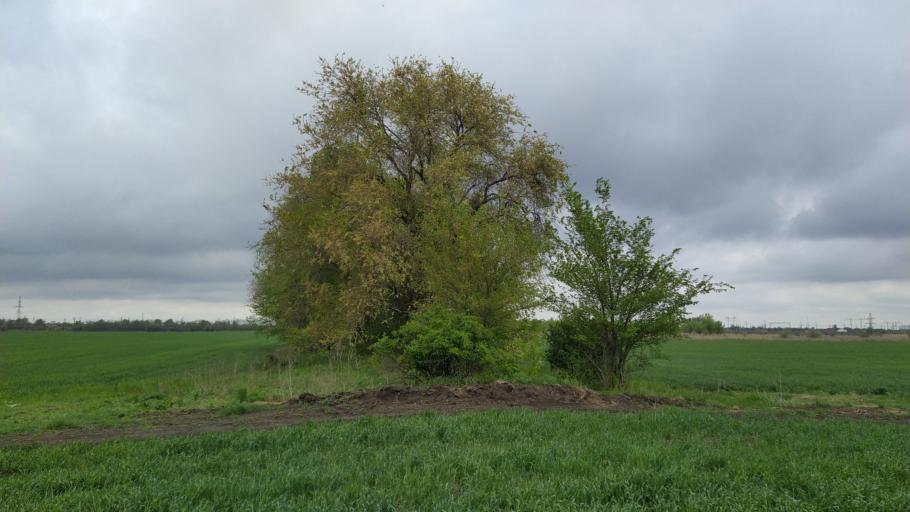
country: RU
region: Rostov
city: Bataysk
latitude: 47.1240
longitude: 39.7228
